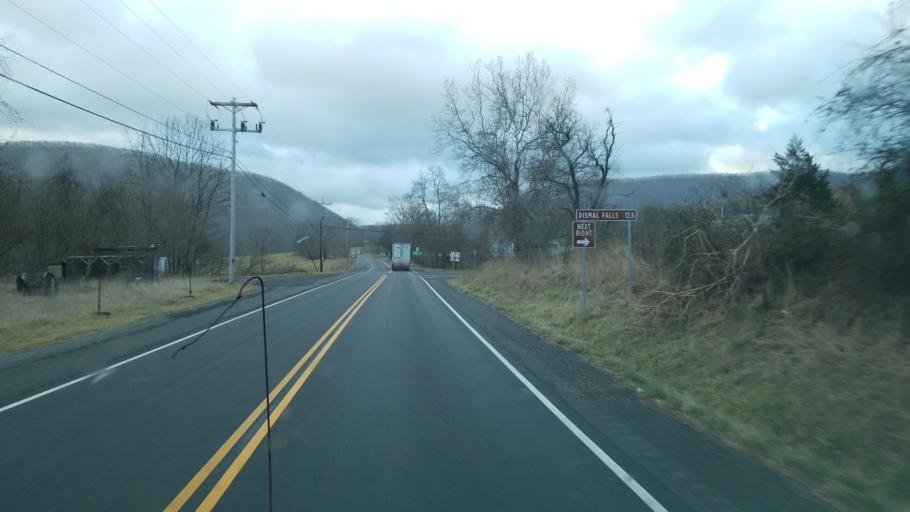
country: US
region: Virginia
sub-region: Giles County
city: Pearisburg
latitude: 37.2185
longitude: -80.7391
